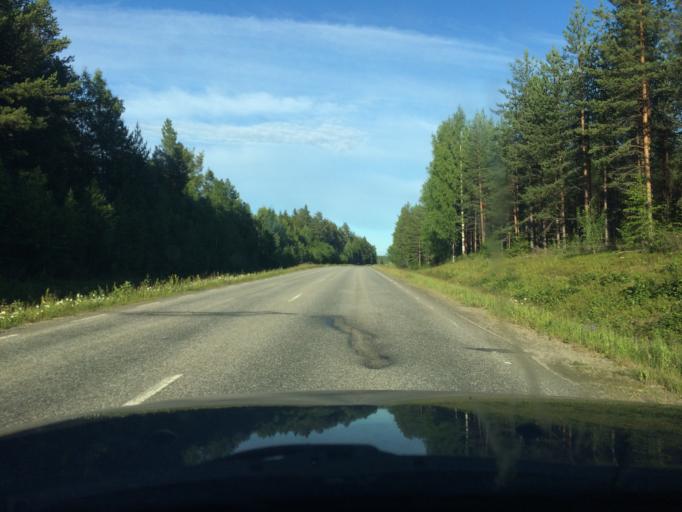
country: SE
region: Norrbotten
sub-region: Pitea Kommun
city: Bergsviken
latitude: 65.3155
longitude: 21.3049
